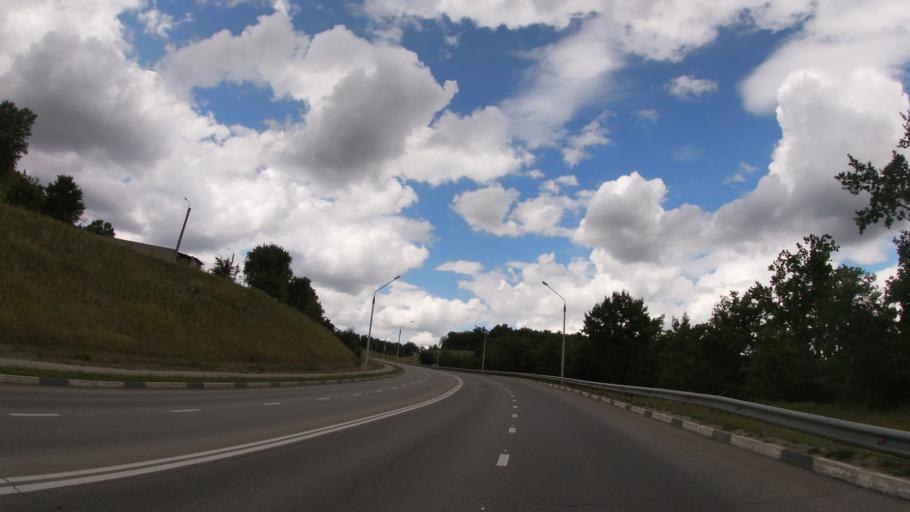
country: RU
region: Belgorod
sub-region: Belgorodskiy Rayon
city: Belgorod
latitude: 50.6204
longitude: 36.6161
